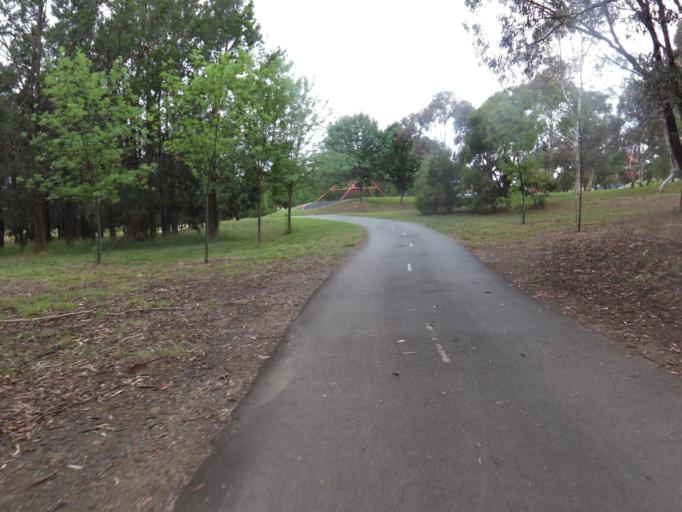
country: AU
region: Australian Capital Territory
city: Kaleen
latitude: -35.1790
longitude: 149.1291
